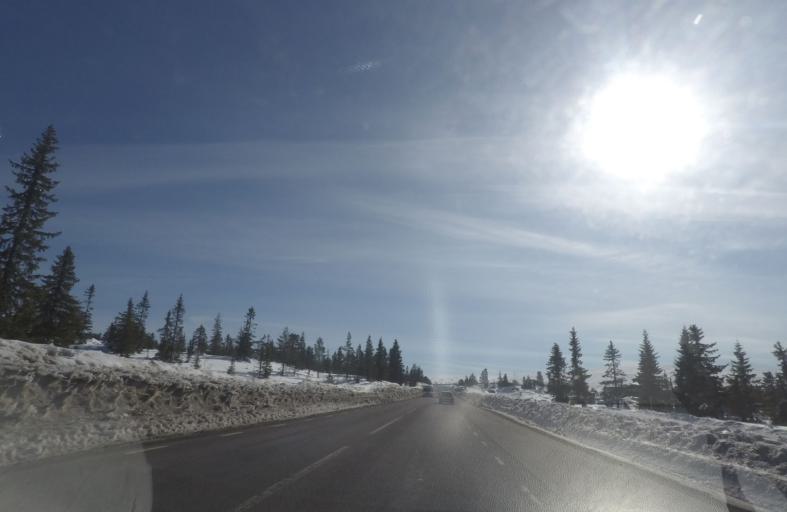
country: SE
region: Dalarna
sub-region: Malung-Saelens kommun
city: Malung
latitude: 61.1620
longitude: 13.1086
